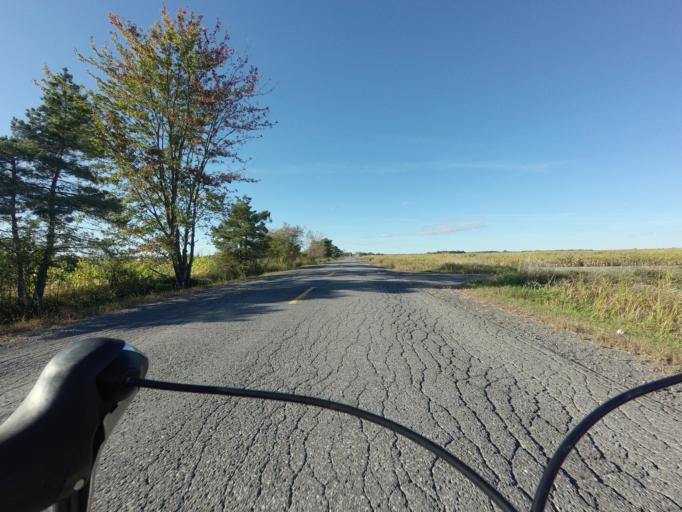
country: CA
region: Ontario
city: Bells Corners
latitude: 45.2011
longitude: -75.7909
